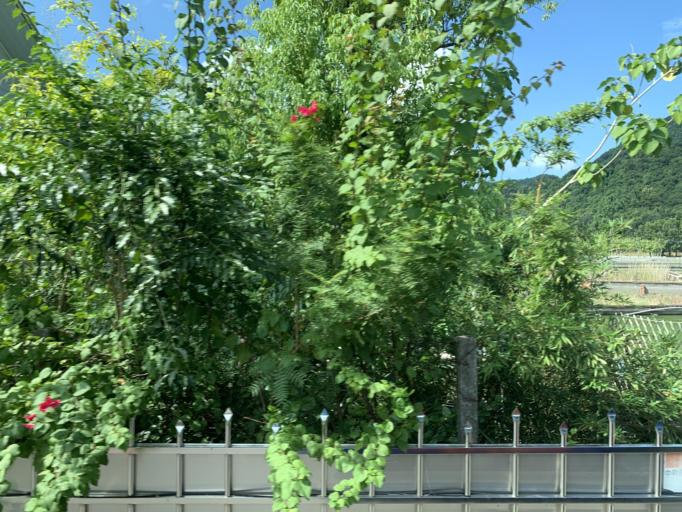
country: TW
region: Taiwan
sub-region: Pingtung
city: Pingtung
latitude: 22.9004
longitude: 120.5172
